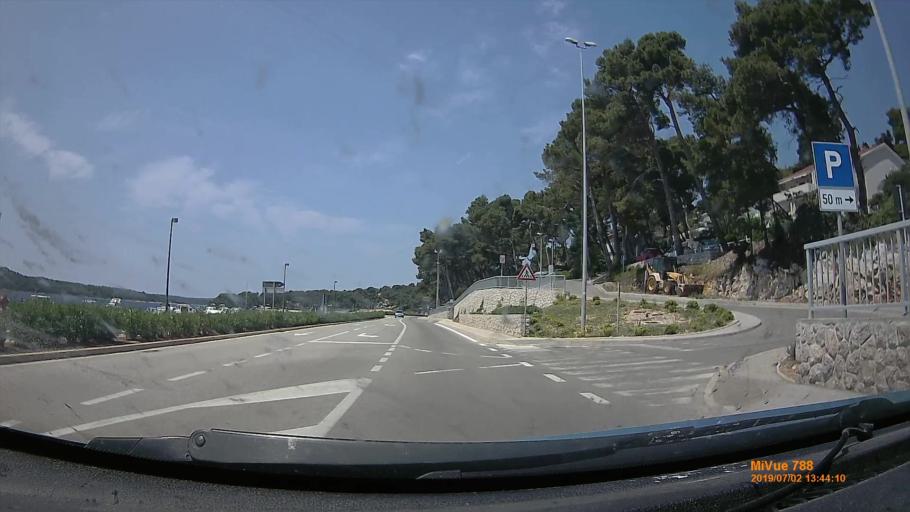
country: HR
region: Primorsko-Goranska
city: Mali Losinj
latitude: 44.5498
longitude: 14.4514
